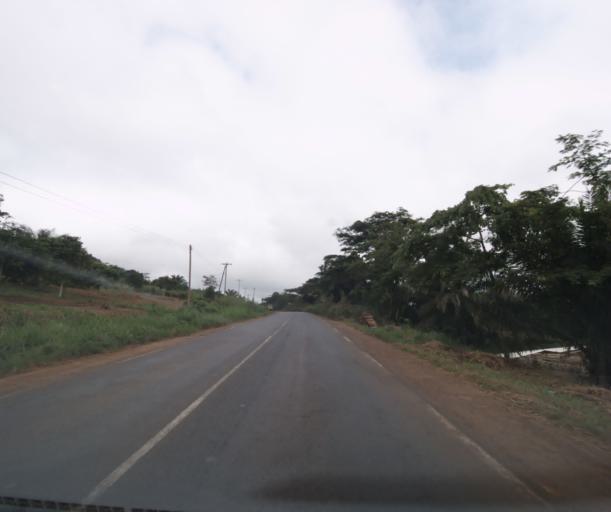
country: CM
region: Centre
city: Mbankomo
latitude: 3.7913
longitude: 11.4122
